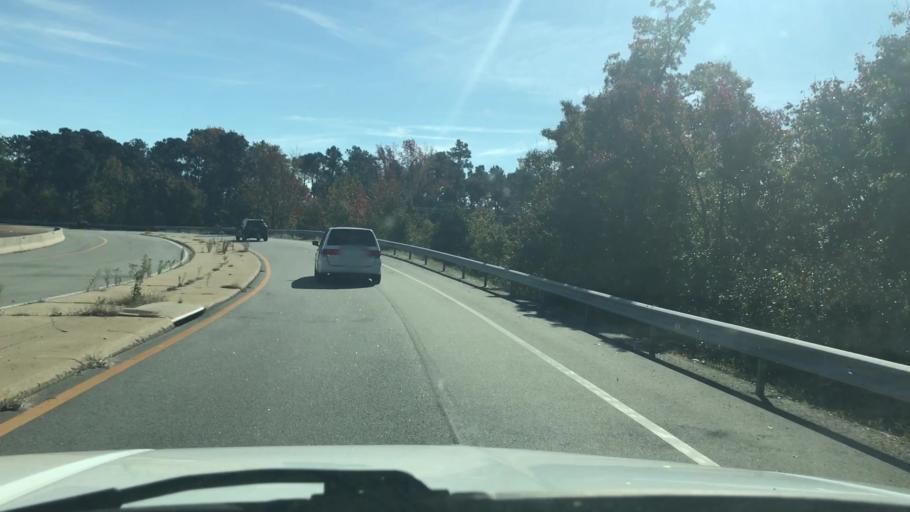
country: US
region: Virginia
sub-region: Henrico County
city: Short Pump
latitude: 37.6471
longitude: -77.5952
